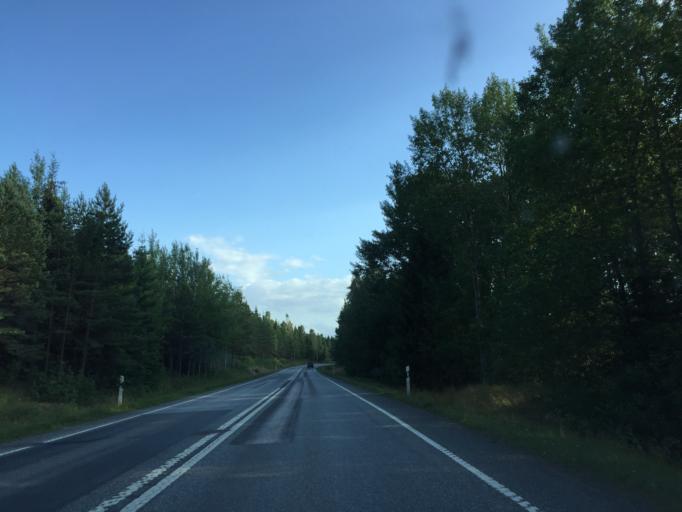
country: SE
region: OEstergoetland
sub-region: Motala Kommun
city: Ryd
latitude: 58.6634
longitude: 14.9653
